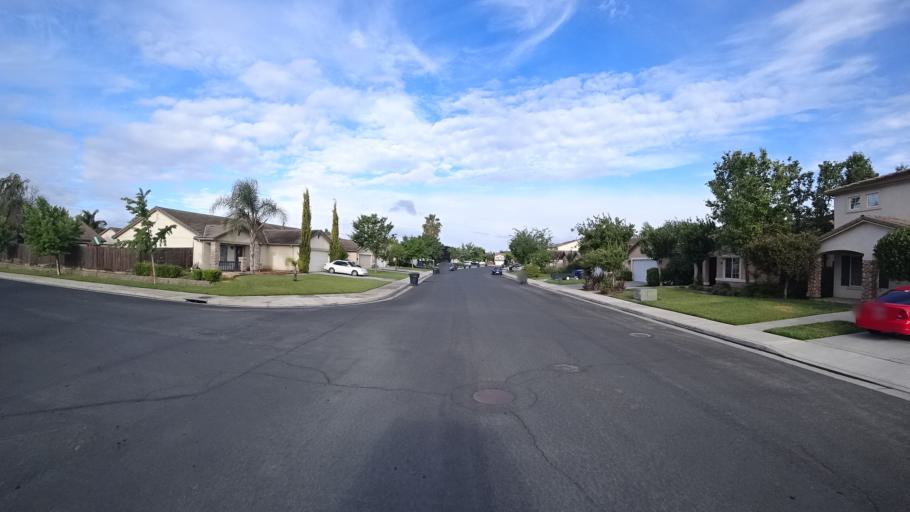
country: US
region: California
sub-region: Kings County
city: Hanford
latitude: 36.3440
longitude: -119.6790
